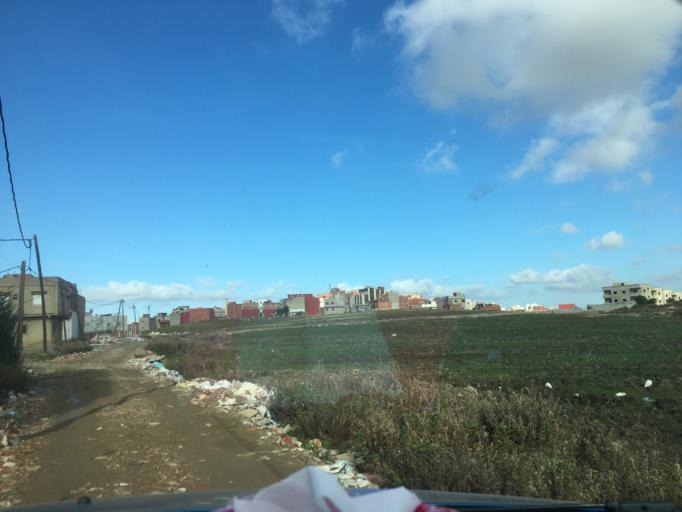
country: MA
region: Tanger-Tetouan
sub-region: Tanger-Assilah
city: Tangier
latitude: 35.7115
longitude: -5.8142
